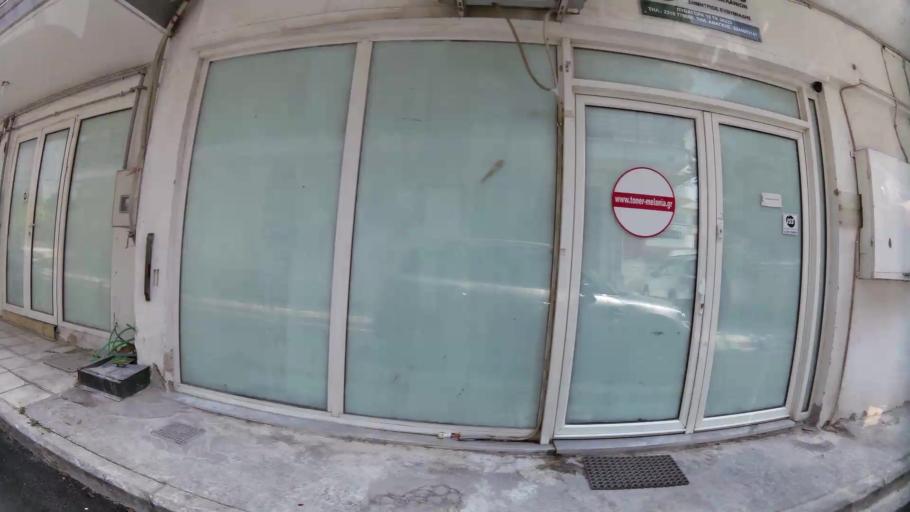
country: GR
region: Central Macedonia
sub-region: Nomos Thessalonikis
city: Menemeni
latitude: 40.6635
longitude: 22.9034
